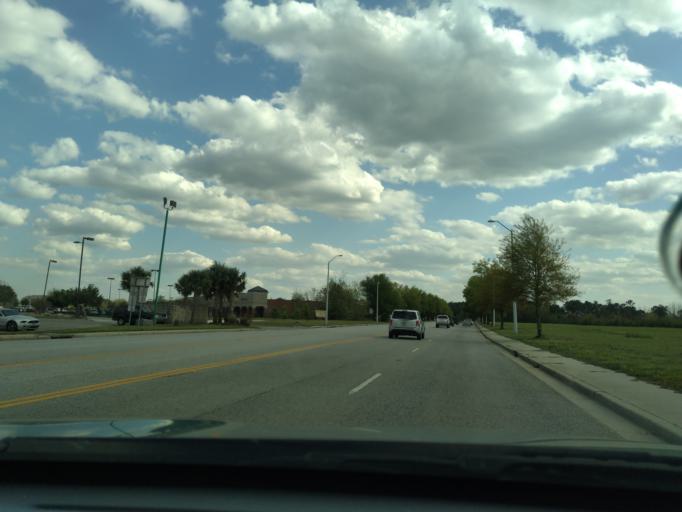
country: US
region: South Carolina
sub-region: Florence County
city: Florence
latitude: 34.1633
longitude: -79.7601
